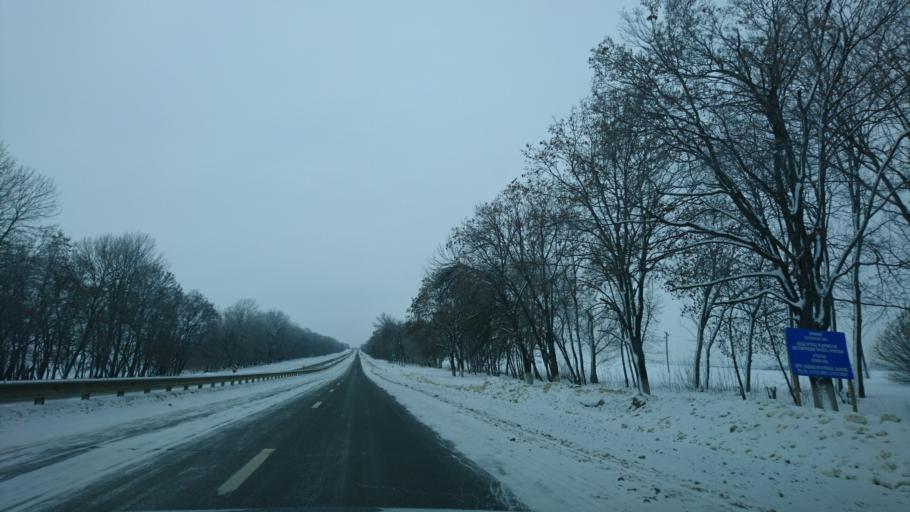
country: RU
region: Belgorod
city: Mayskiy
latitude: 50.4324
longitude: 36.3871
